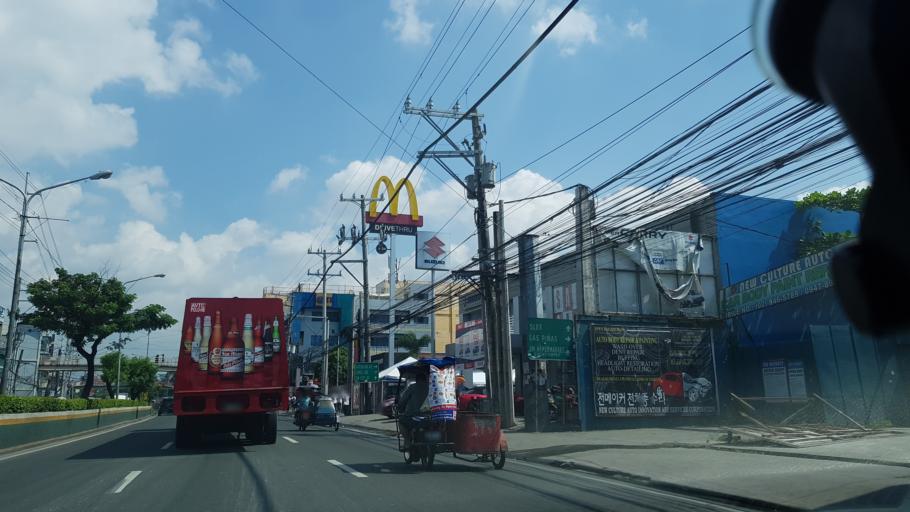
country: PH
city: Sambayanihan People's Village
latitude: 14.4765
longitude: 120.9997
